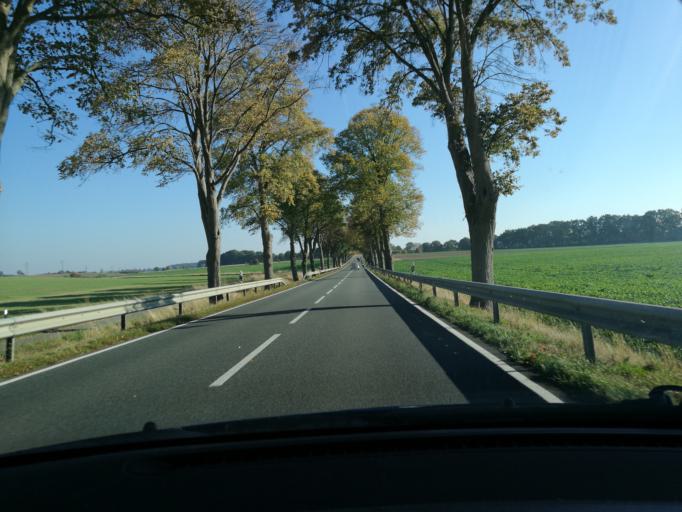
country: DE
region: Lower Saxony
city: Nahrendorf
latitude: 53.1660
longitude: 10.7914
